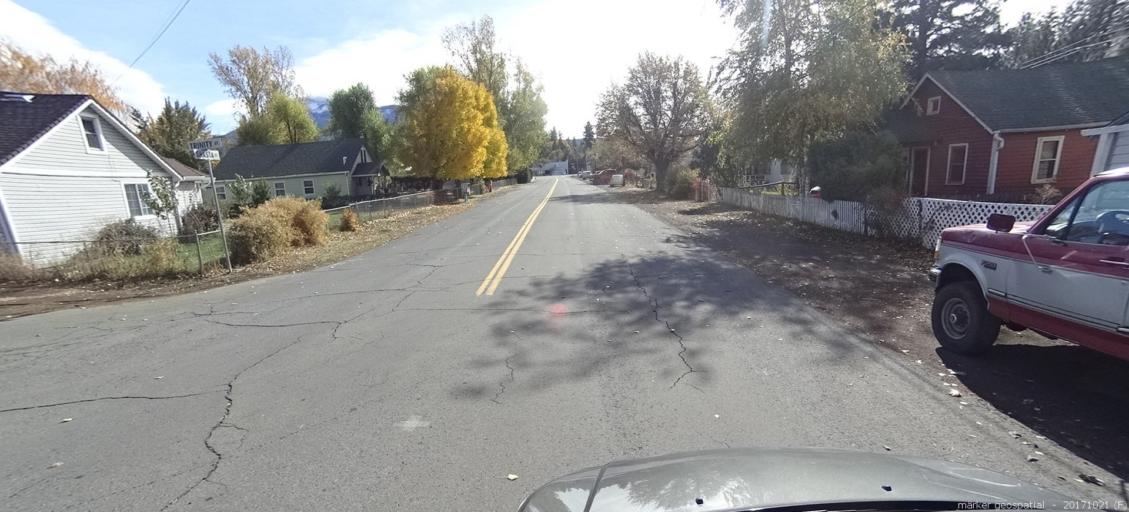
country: US
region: California
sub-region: Shasta County
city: Burney
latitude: 40.8835
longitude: -121.6707
